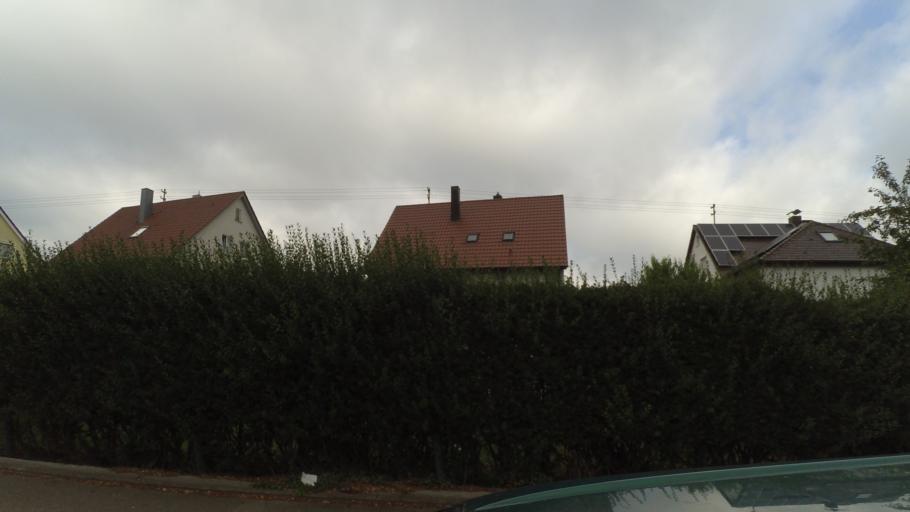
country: DE
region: Baden-Wuerttemberg
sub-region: Tuebingen Region
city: Langenau
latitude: 48.4890
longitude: 10.1170
